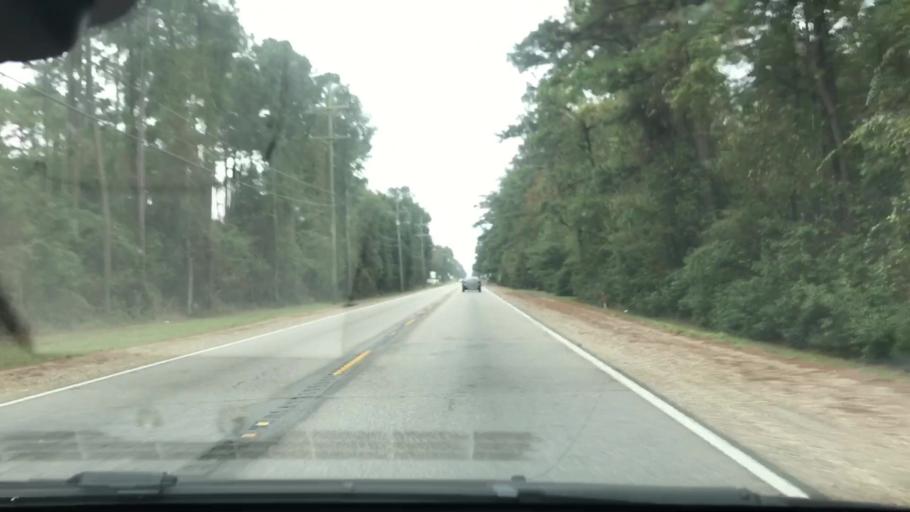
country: US
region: Louisiana
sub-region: Saint Tammany Parish
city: Pearl River
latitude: 30.3482
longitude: -89.7556
